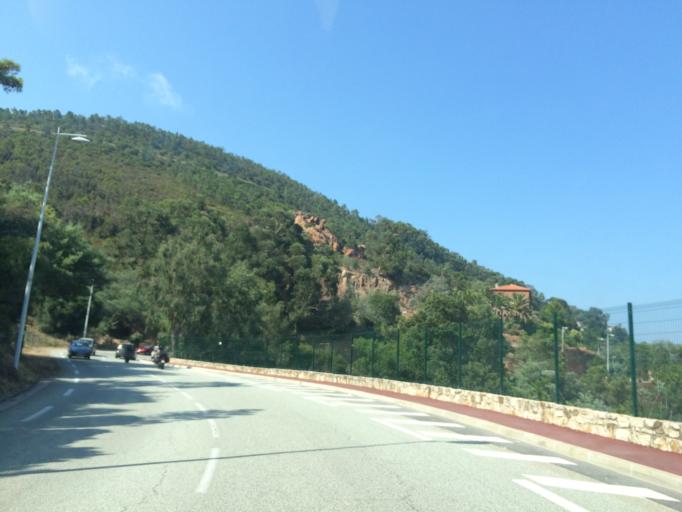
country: FR
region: Provence-Alpes-Cote d'Azur
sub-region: Departement des Alpes-Maritimes
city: Theoule-sur-Mer
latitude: 43.4950
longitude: 6.9451
